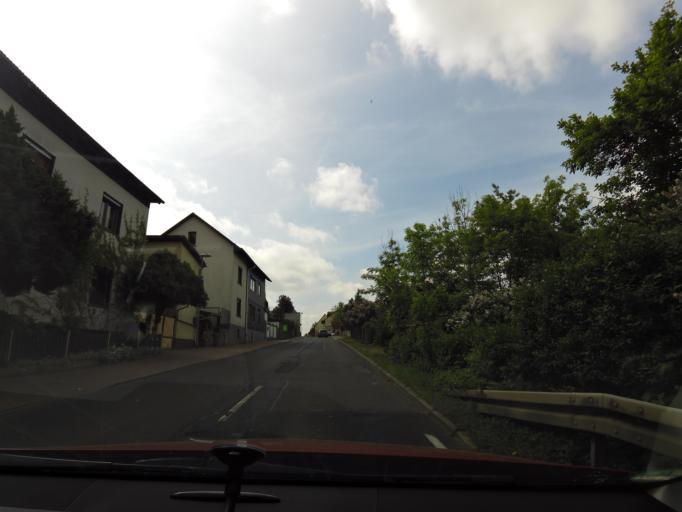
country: DE
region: Thuringia
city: Mihla
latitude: 51.0808
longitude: 10.3376
